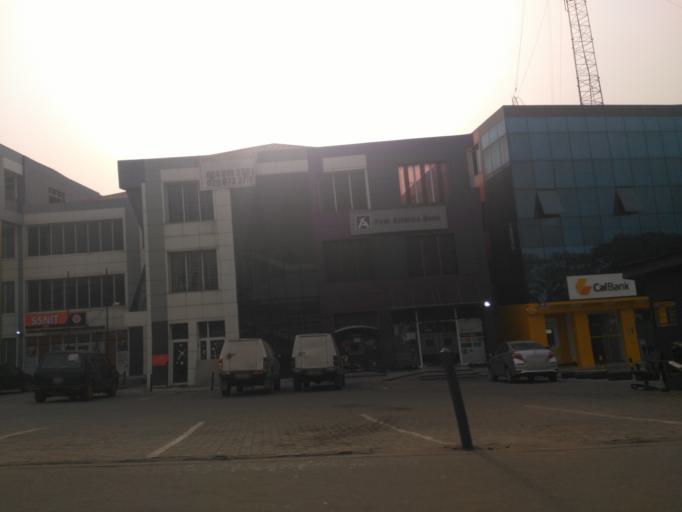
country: GH
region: Ashanti
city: Tafo
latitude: 6.7186
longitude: -1.6313
